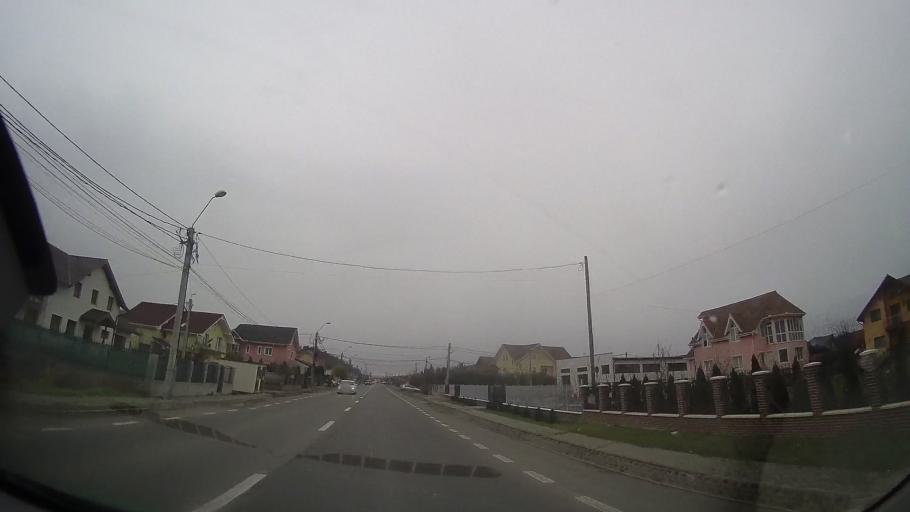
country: RO
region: Mures
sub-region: Comuna Santana de Mures
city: Santana de Mures
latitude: 46.5892
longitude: 24.5357
